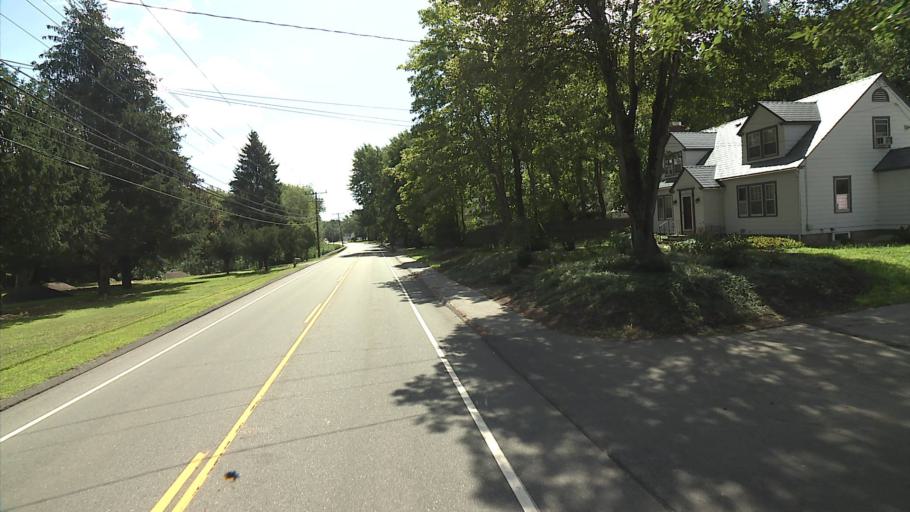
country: US
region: Connecticut
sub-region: New London County
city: Niantic
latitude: 41.3632
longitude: -72.1805
